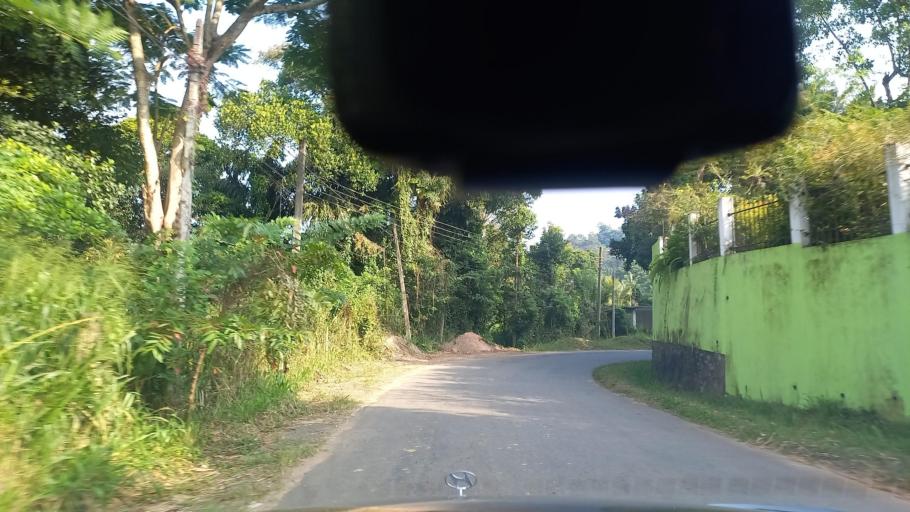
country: LK
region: Central
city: Gampola
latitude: 7.2213
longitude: 80.6056
